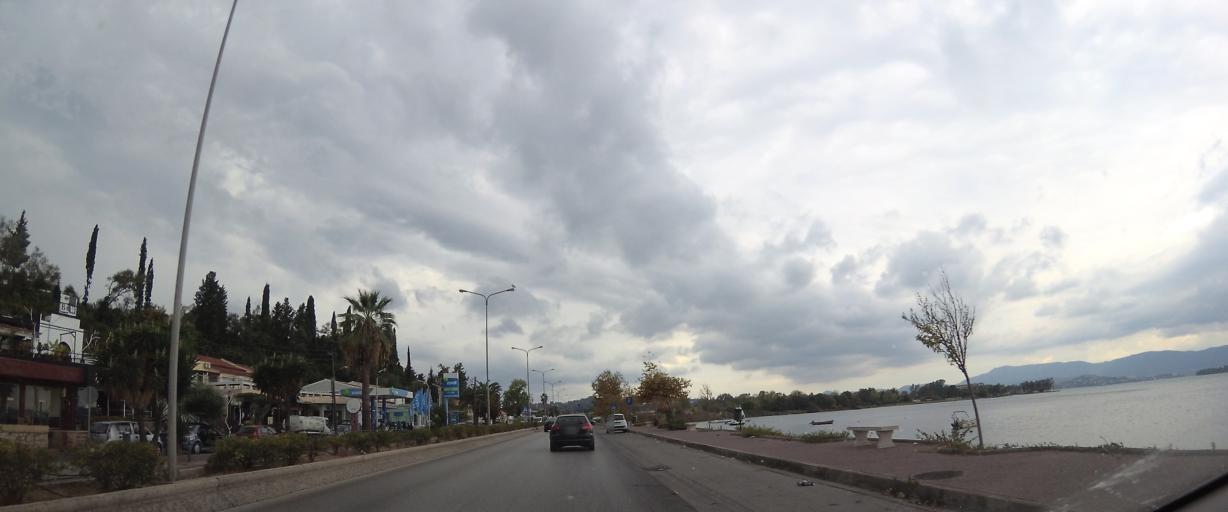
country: GR
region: Ionian Islands
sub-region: Nomos Kerkyras
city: Alepou
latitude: 39.6302
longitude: 19.8948
